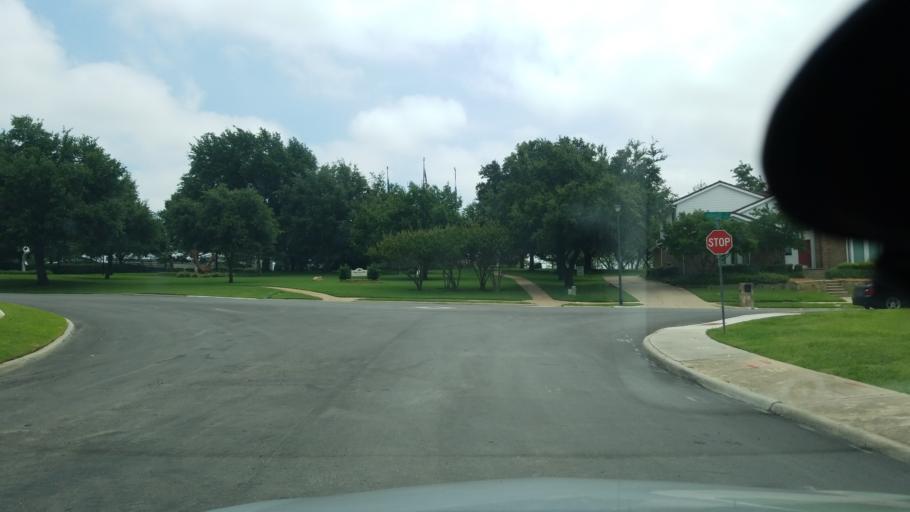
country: US
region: Texas
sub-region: Dallas County
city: Irving
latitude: 32.8520
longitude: -96.9399
